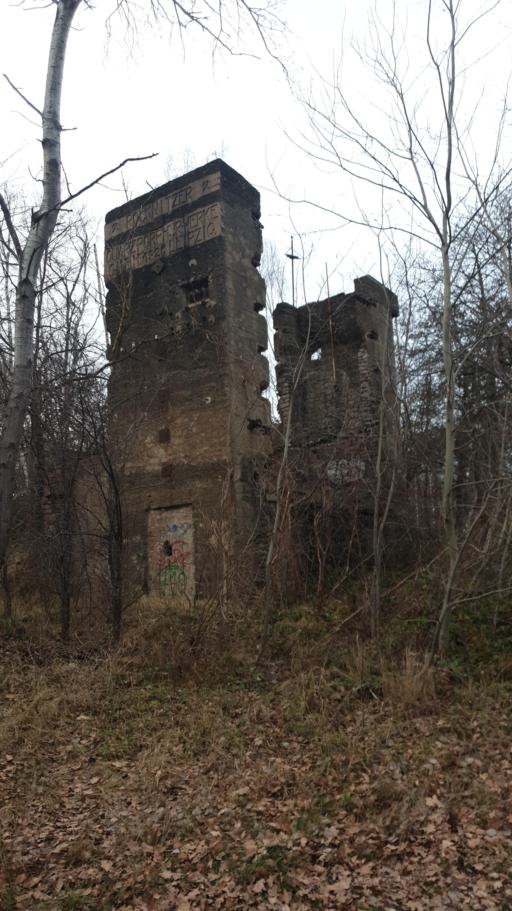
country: DE
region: Saxony
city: Hohburg
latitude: 51.4266
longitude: 12.7837
